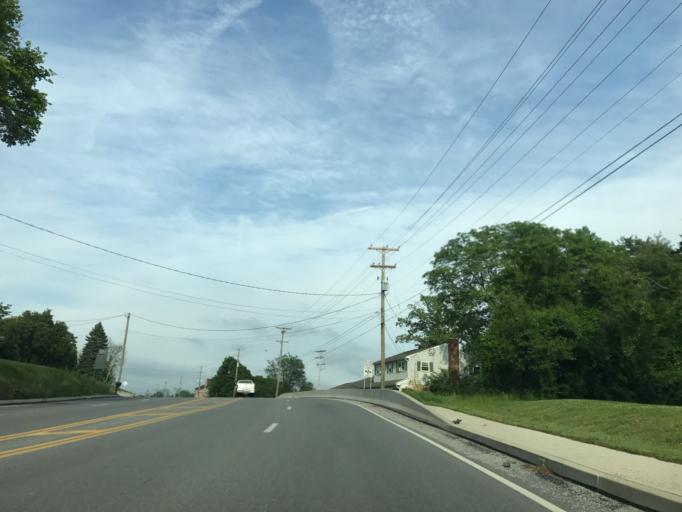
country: US
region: Pennsylvania
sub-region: York County
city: East York
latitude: 39.9583
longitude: -76.6714
